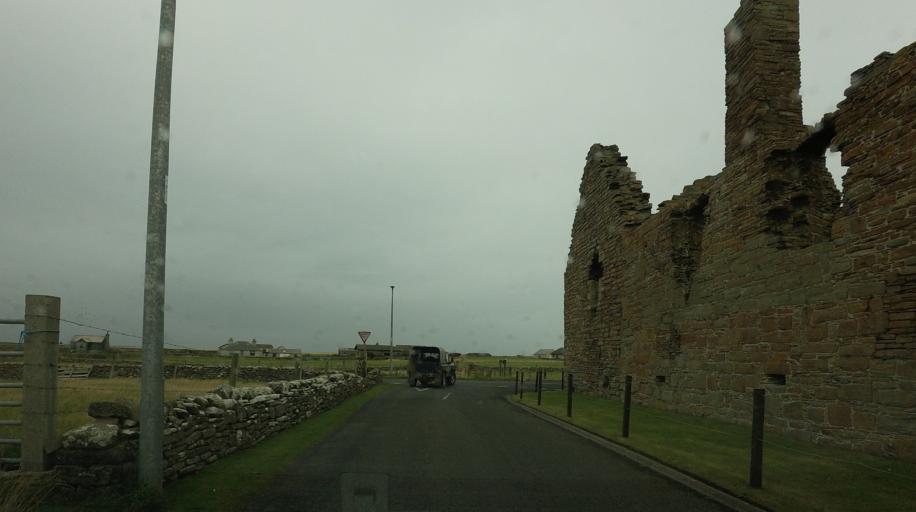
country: GB
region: Scotland
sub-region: Orkney Islands
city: Stromness
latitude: 59.1302
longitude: -3.3158
